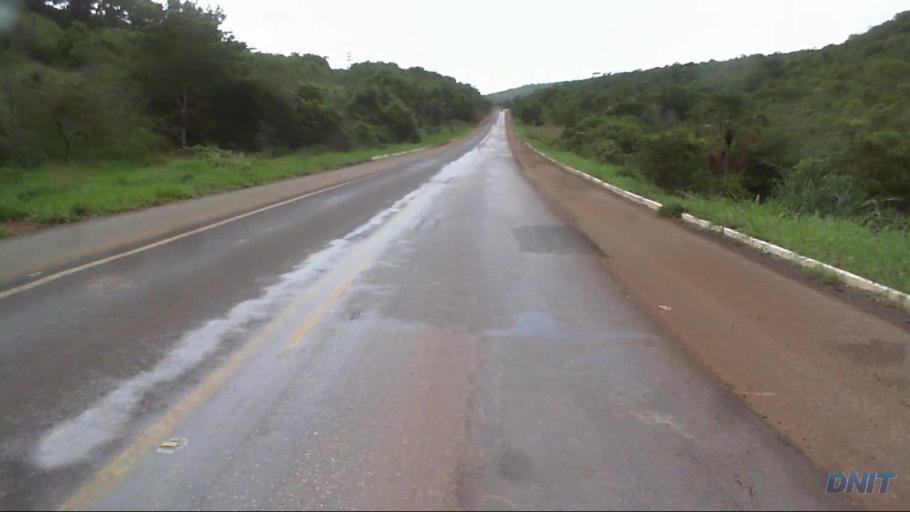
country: BR
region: Goias
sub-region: Barro Alto
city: Barro Alto
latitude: -14.9199
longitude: -48.9515
